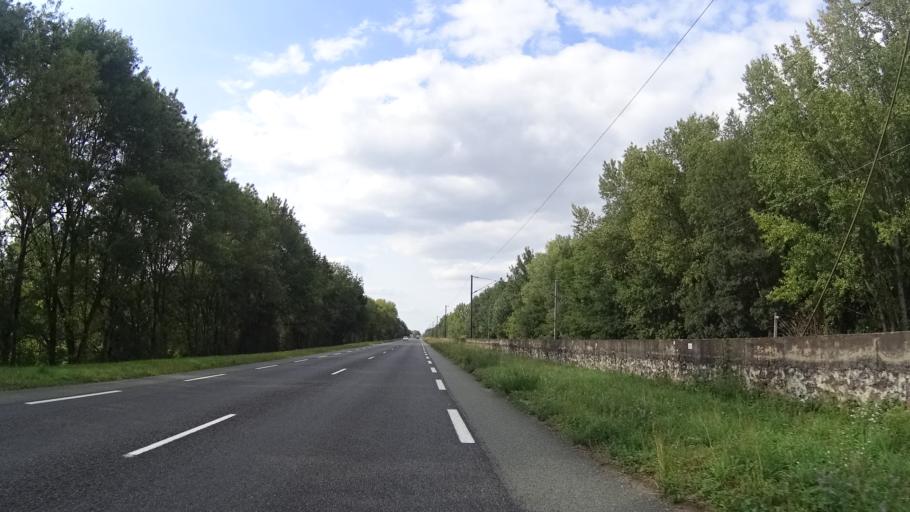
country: FR
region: Pays de la Loire
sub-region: Departement de Maine-et-Loire
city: Saint-Martin-de-la-Place
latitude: 47.2957
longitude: -0.1148
